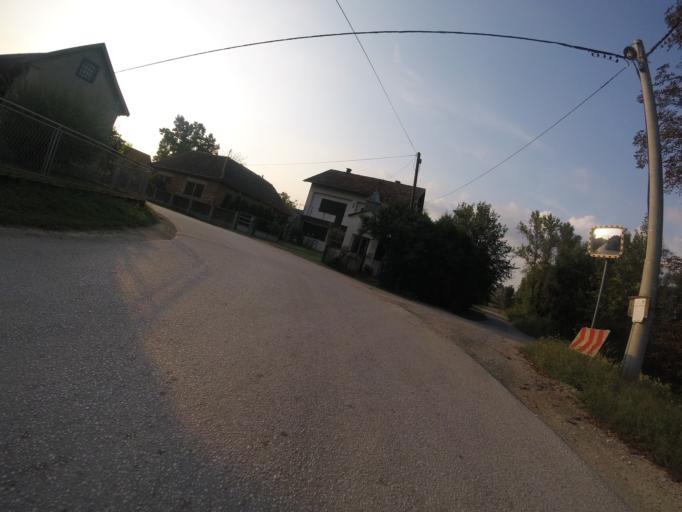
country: HR
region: Zagrebacka
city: Kuce
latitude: 45.7304
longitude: 16.1967
